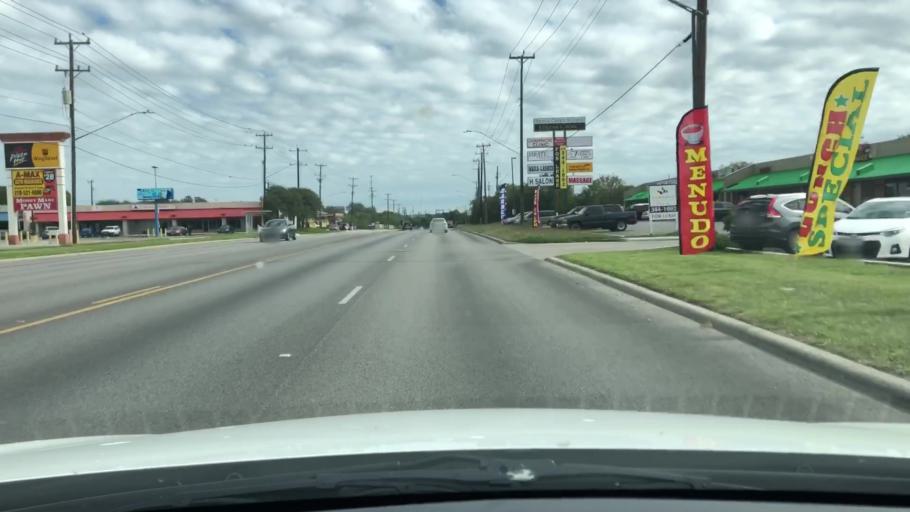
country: US
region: Texas
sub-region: Bexar County
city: Leon Valley
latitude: 29.4794
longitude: -98.6571
